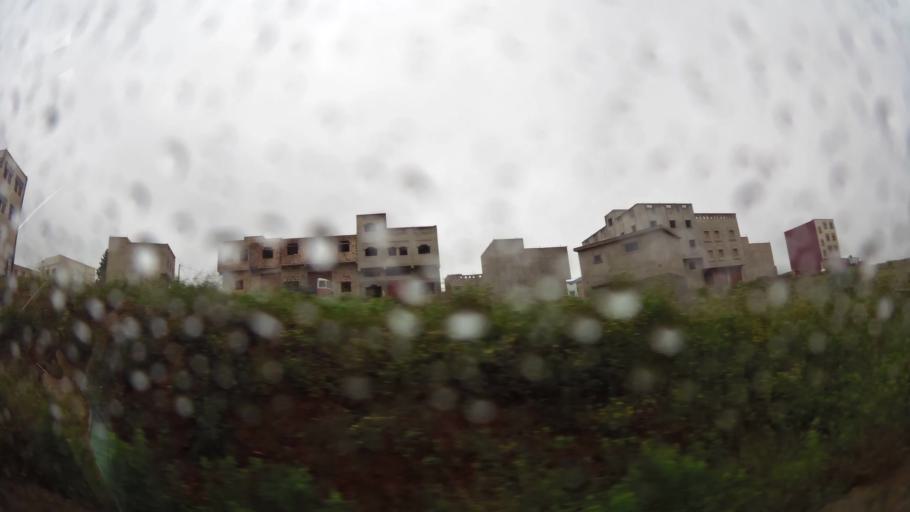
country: MA
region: Oriental
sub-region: Nador
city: Boudinar
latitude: 35.1222
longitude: -3.6371
